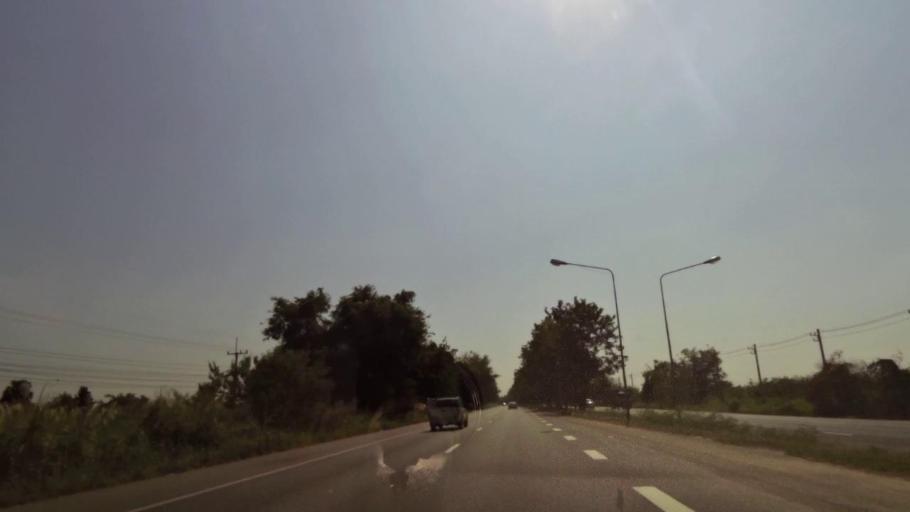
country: TH
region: Nakhon Sawan
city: Kao Liao
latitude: 15.9291
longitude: 100.1124
